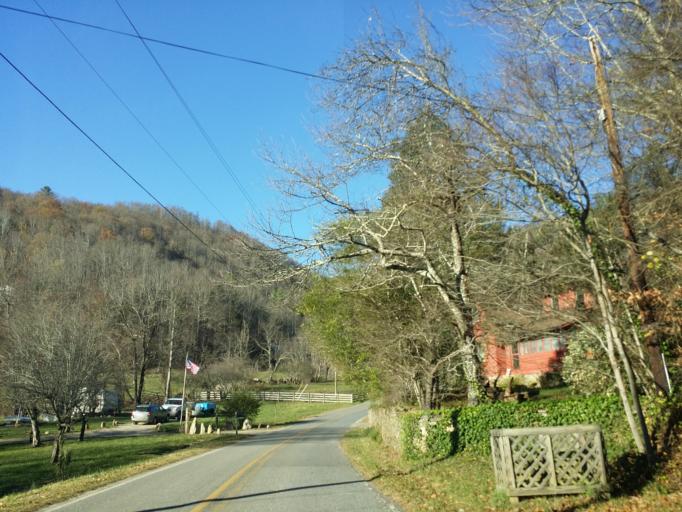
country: US
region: North Carolina
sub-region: Buncombe County
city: Swannanoa
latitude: 35.6359
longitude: -82.4162
